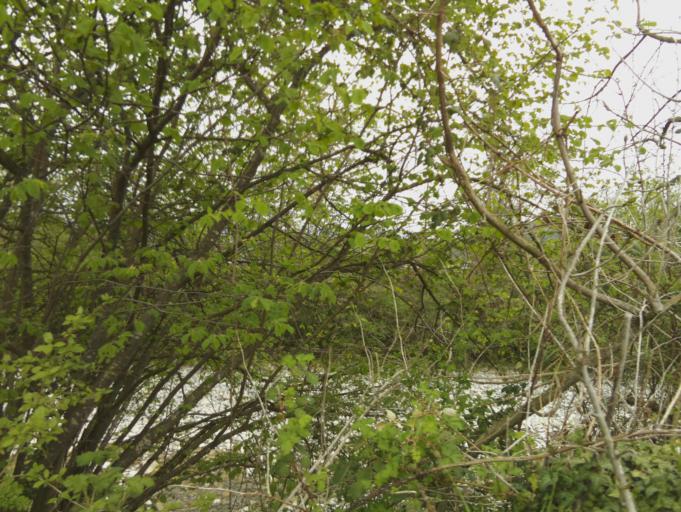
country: CH
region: Schwyz
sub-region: Bezirk March
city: Lachen
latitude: 47.1895
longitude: 8.8760
